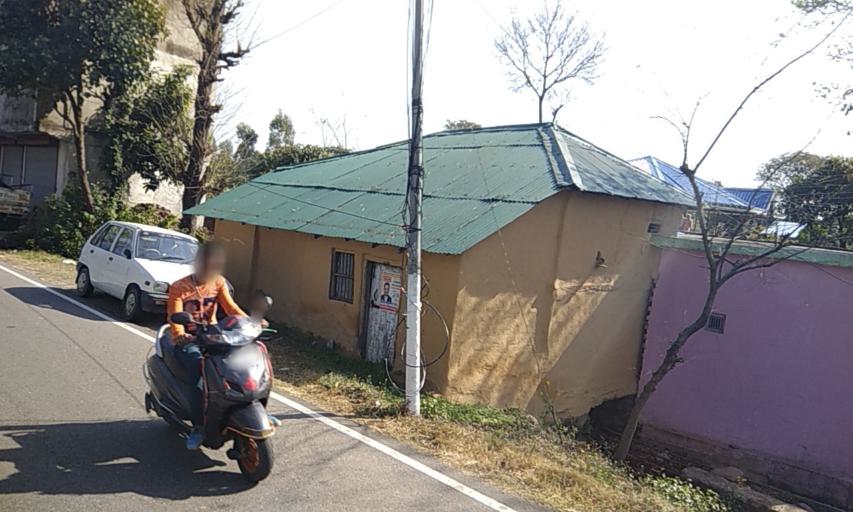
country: IN
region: Himachal Pradesh
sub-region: Kangra
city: Dharmsala
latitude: 32.1654
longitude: 76.3954
